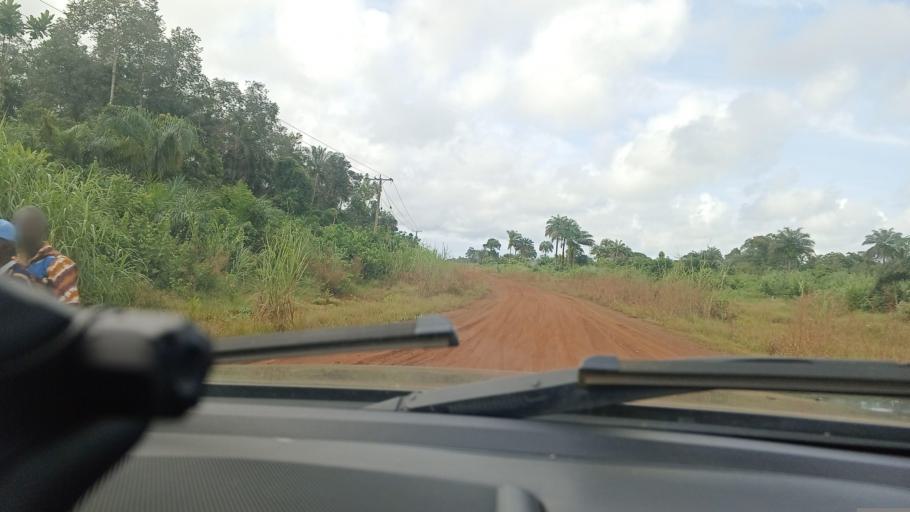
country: LR
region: Grand Cape Mount
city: Robertsport
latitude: 6.6798
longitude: -11.1357
